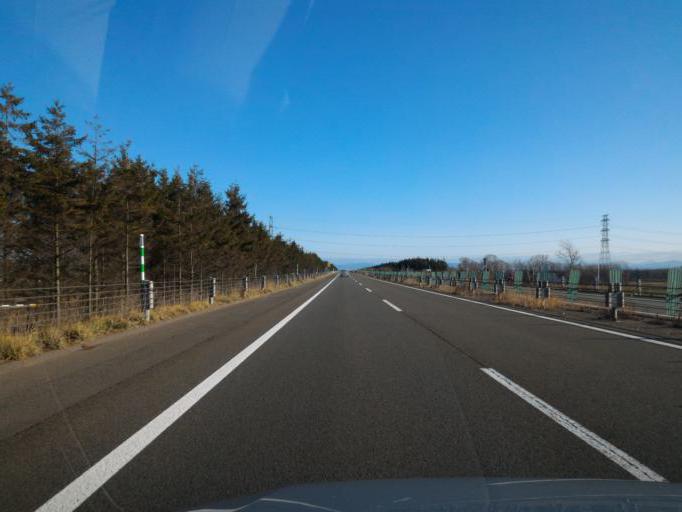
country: JP
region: Hokkaido
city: Ebetsu
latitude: 43.1178
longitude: 141.6246
